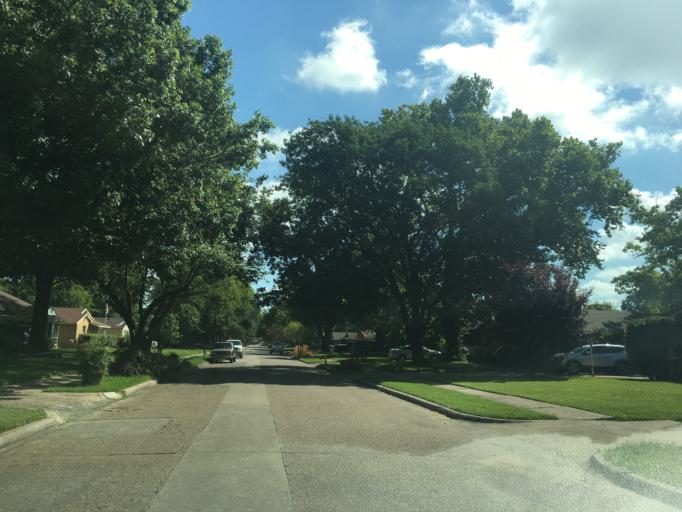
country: US
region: Texas
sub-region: Dallas County
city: Garland
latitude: 32.8463
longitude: -96.6619
